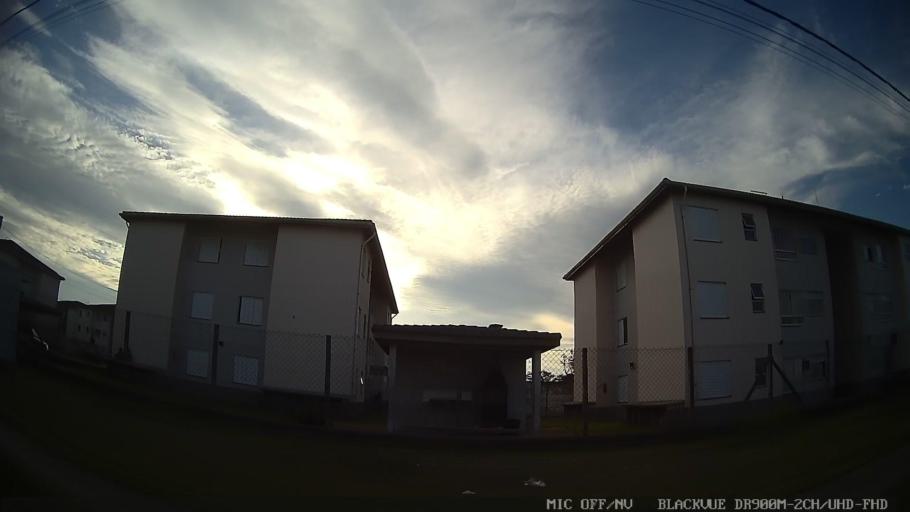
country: BR
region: Sao Paulo
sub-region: Itanhaem
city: Itanhaem
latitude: -24.1521
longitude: -46.7922
